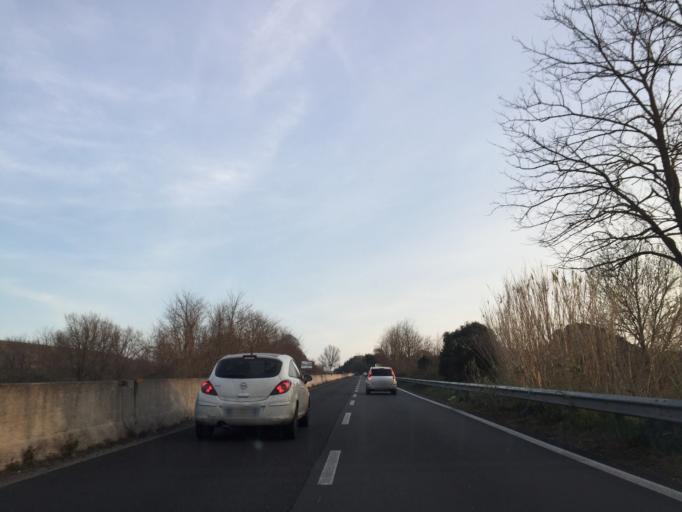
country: IT
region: Latium
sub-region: Citta metropolitana di Roma Capitale
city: Campagnano di Roma
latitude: 42.1406
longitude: 12.3515
